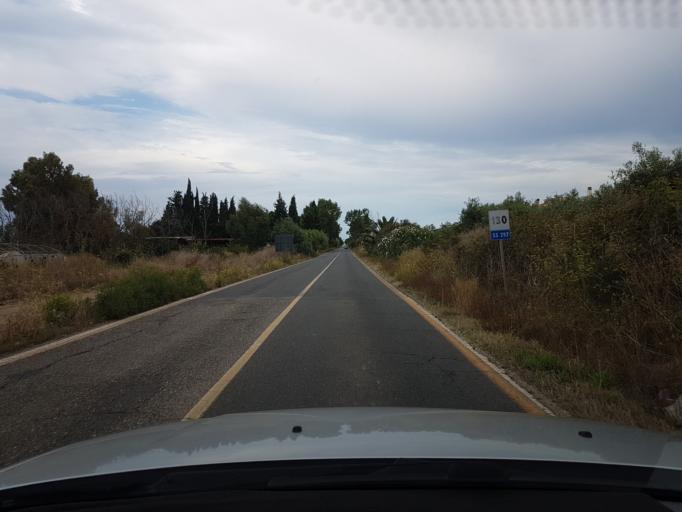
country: IT
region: Sardinia
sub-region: Provincia di Oristano
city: Nuraxinieddu
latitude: 39.9383
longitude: 8.5976
